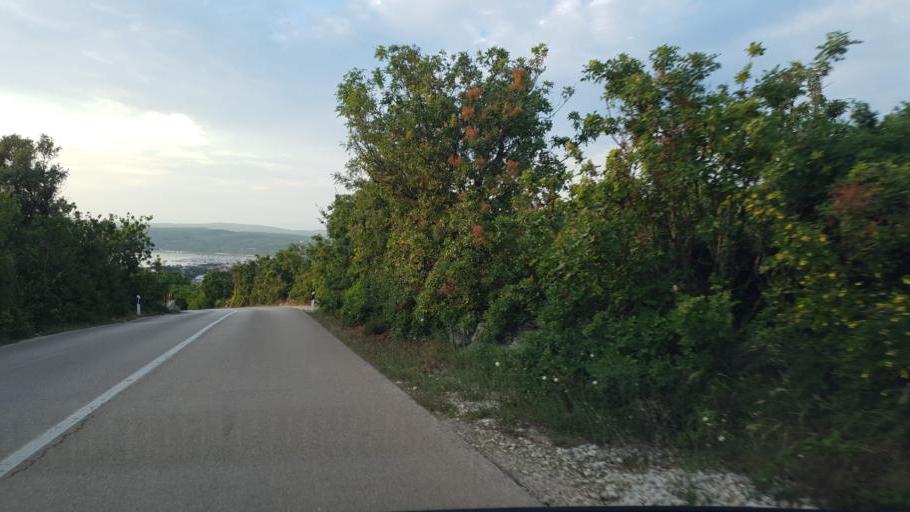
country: HR
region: Primorsko-Goranska
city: Punat
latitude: 45.0062
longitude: 14.6330
